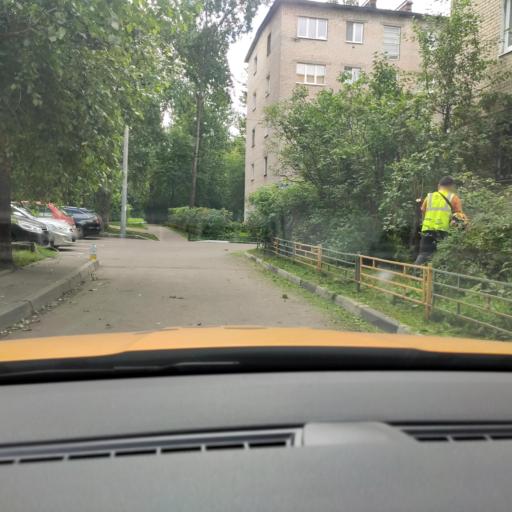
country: RU
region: Moskovskaya
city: Balashikha
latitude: 55.8001
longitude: 37.9558
